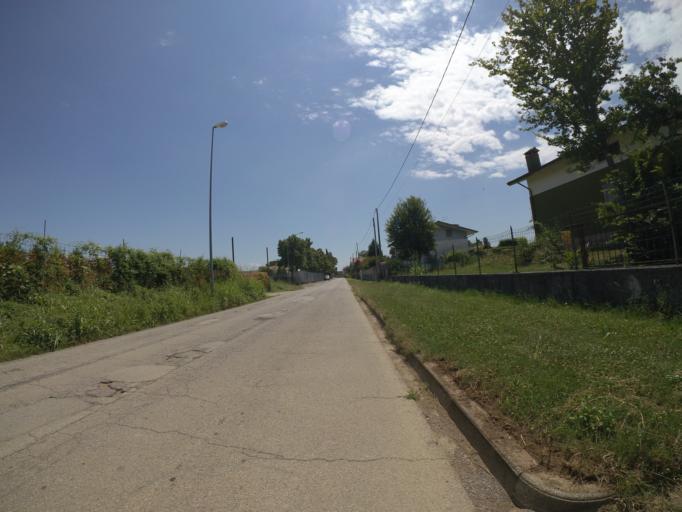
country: IT
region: Friuli Venezia Giulia
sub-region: Provincia di Udine
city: Lestizza
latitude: 45.9739
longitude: 13.1569
